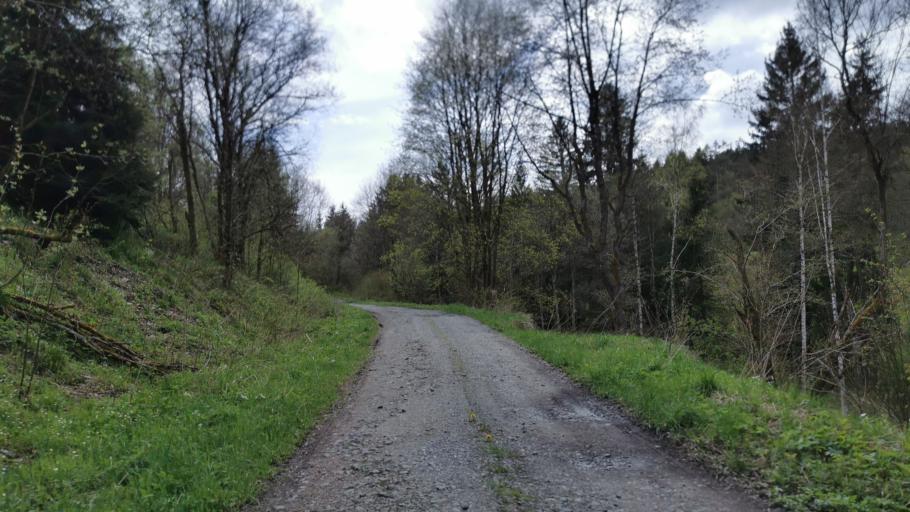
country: DE
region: Bavaria
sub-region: Upper Franconia
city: Ludwigsstadt
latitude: 50.4724
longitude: 11.4204
